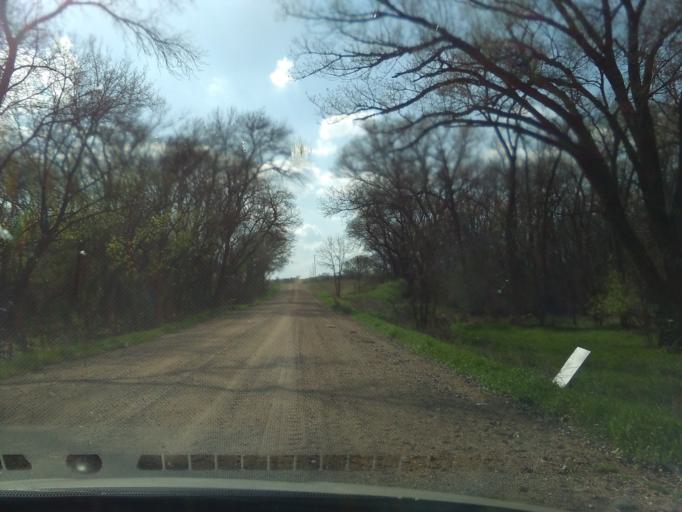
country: US
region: Nebraska
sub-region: Webster County
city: Red Cloud
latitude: 40.0315
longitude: -98.4219
